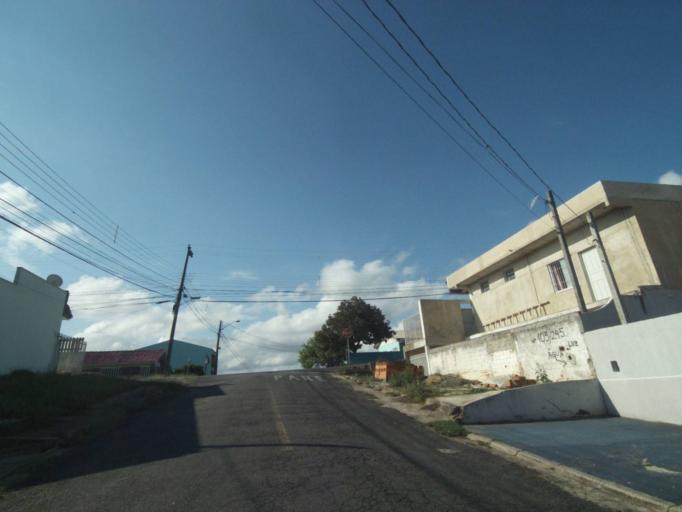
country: BR
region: Parana
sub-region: Curitiba
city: Curitiba
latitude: -25.3950
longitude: -49.3035
